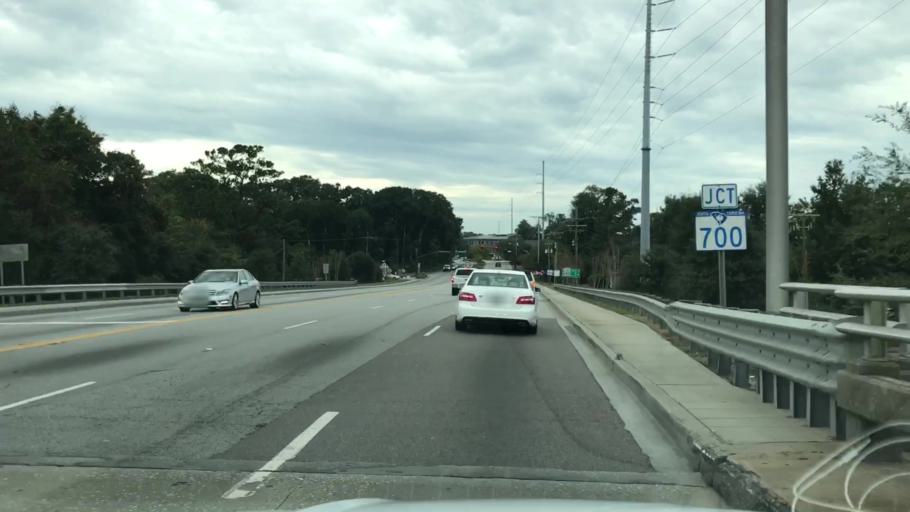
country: US
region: South Carolina
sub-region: Charleston County
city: Charleston
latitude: 32.7655
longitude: -79.9743
